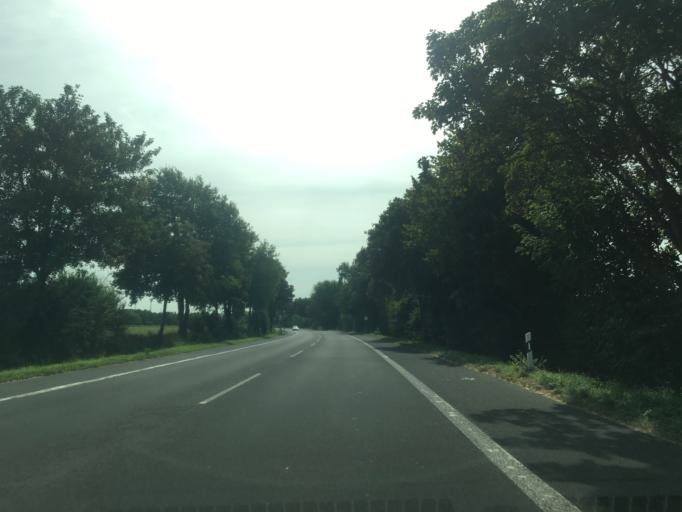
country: DE
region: North Rhine-Westphalia
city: Erkelenz
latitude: 51.0607
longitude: 6.3578
